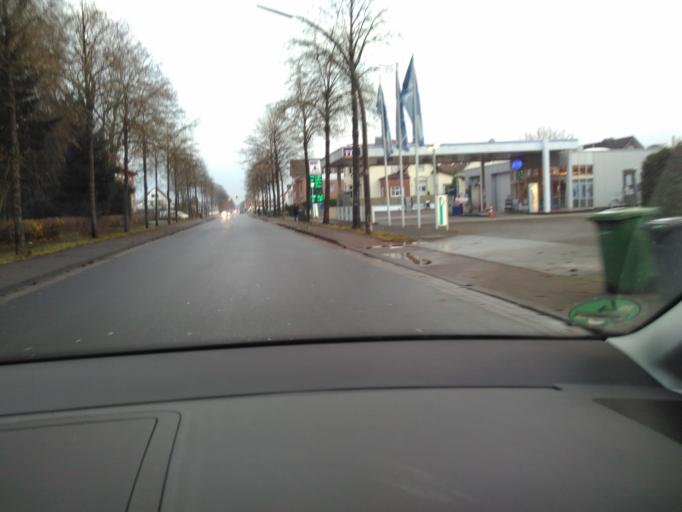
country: DE
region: North Rhine-Westphalia
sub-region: Regierungsbezirk Detmold
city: Rheda-Wiedenbruck
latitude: 51.8405
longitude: 8.3155
